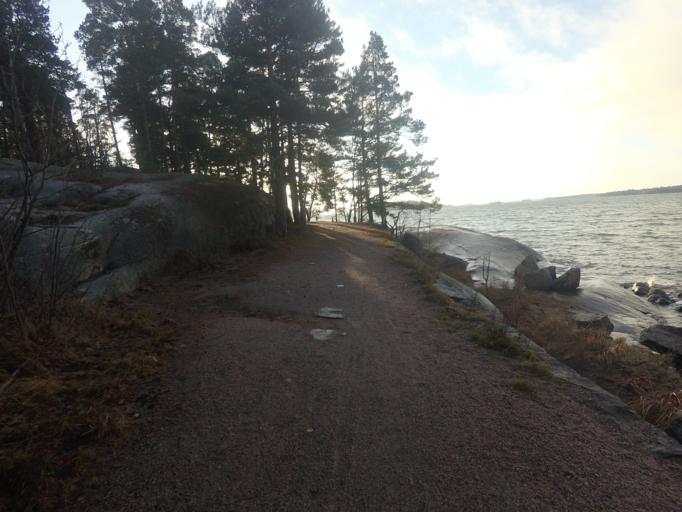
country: FI
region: Uusimaa
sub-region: Helsinki
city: Otaniemi
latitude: 60.1664
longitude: 24.8305
